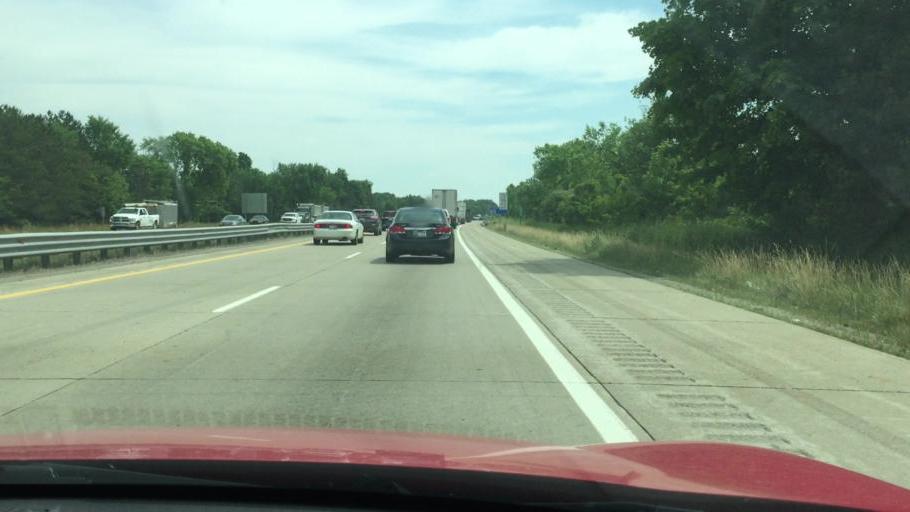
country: US
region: Michigan
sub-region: Genesee County
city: Flint
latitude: 42.9362
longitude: -83.7236
